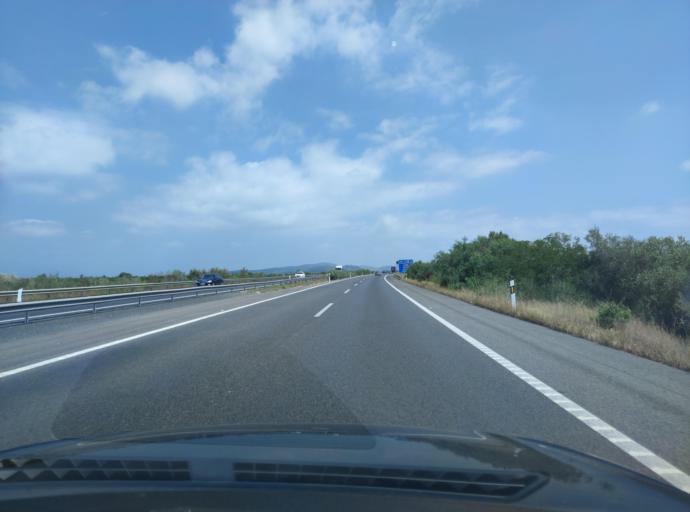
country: ES
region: Catalonia
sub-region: Provincia de Tarragona
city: Ulldecona
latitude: 40.5448
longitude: 0.4195
